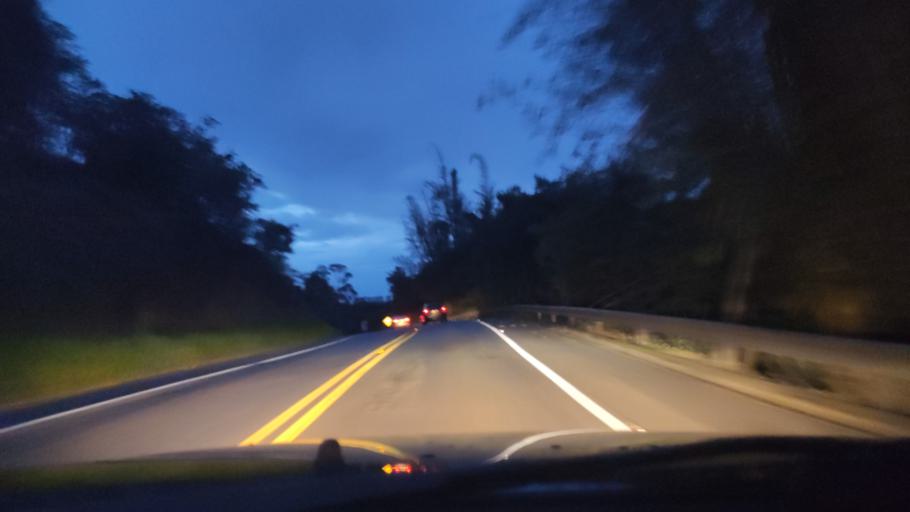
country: BR
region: Sao Paulo
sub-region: Socorro
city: Socorro
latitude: -22.5517
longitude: -46.5719
